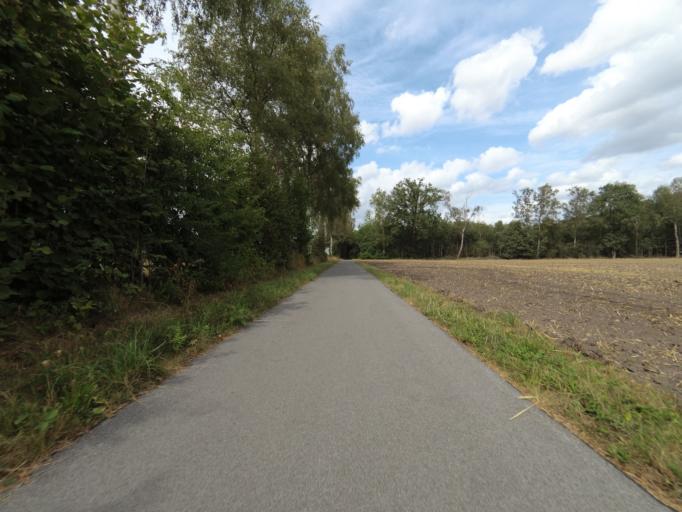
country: DE
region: North Rhine-Westphalia
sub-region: Regierungsbezirk Munster
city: Gronau
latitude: 52.1674
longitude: 6.9781
